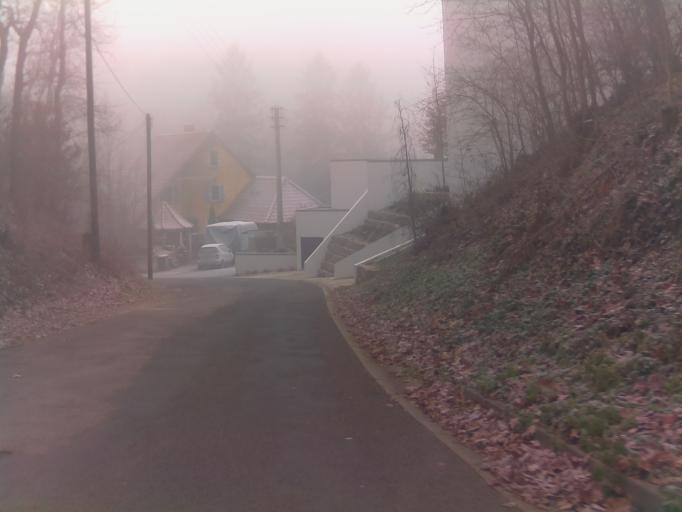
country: DE
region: Bavaria
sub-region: Regierungsbezirk Unterfranken
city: Zeil
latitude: 50.0823
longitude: 10.5770
